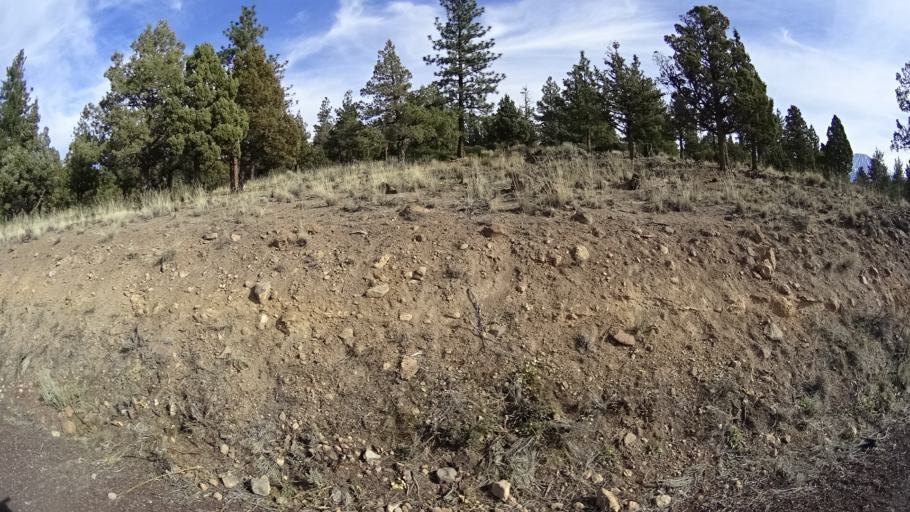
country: US
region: California
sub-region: Siskiyou County
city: Weed
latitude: 41.5161
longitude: -122.3665
